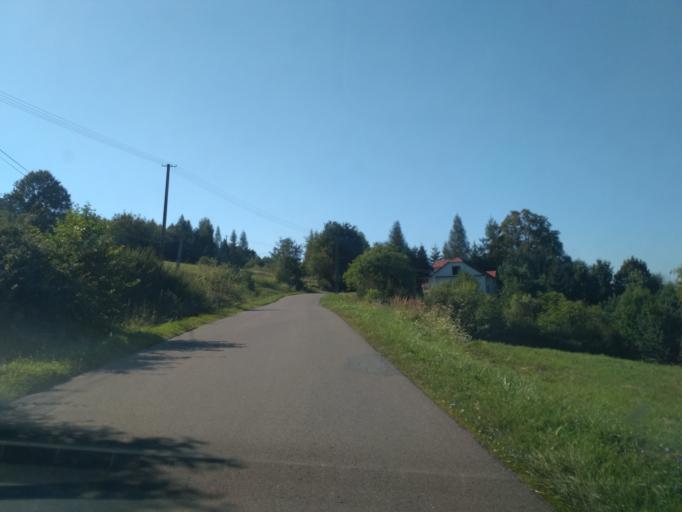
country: PL
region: Subcarpathian Voivodeship
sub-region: Powiat strzyzowski
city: Wysoka Strzyzowska
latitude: 49.8023
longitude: 21.7497
